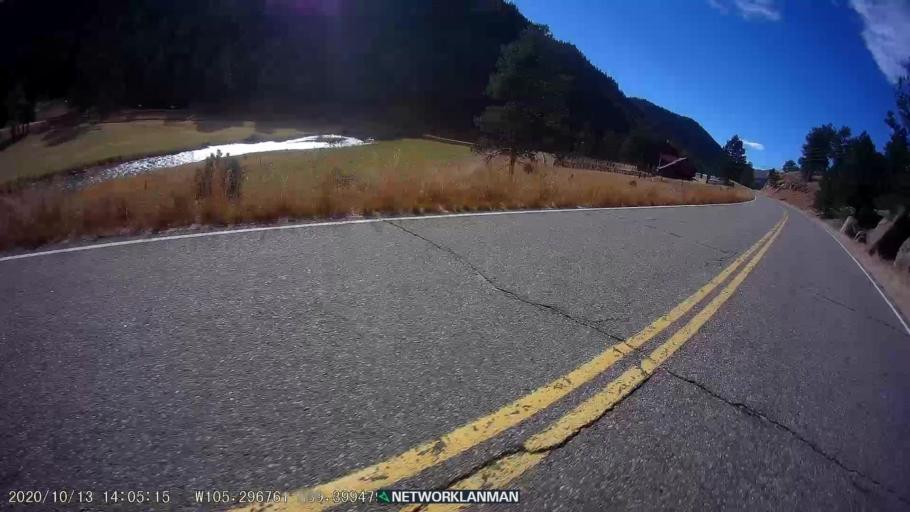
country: US
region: Colorado
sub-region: Douglas County
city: Roxborough Park
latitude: 39.3997
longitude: -105.2973
